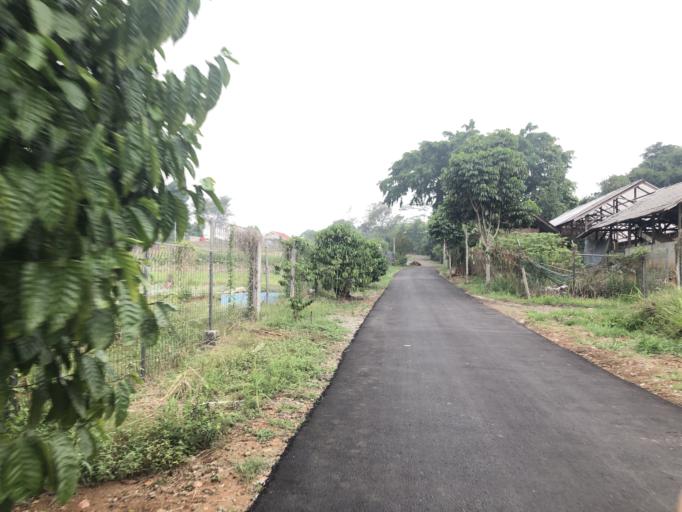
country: ID
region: West Java
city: Ciampea
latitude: -6.5503
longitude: 106.7148
